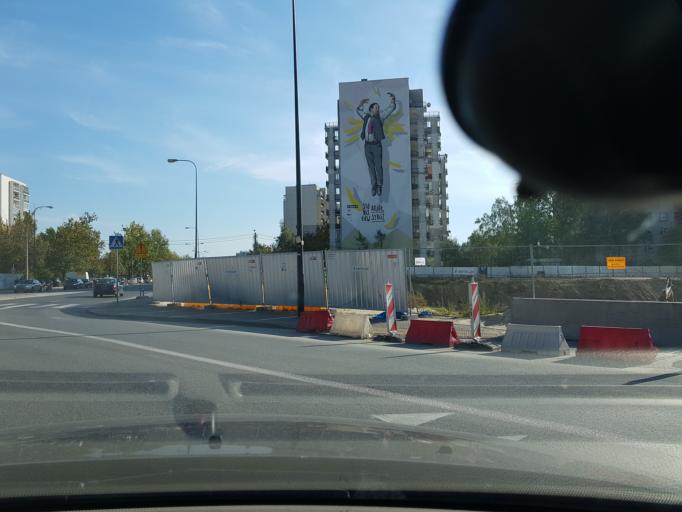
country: PL
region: Masovian Voivodeship
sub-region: Warszawa
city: Ursynow
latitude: 52.1423
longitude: 21.0447
